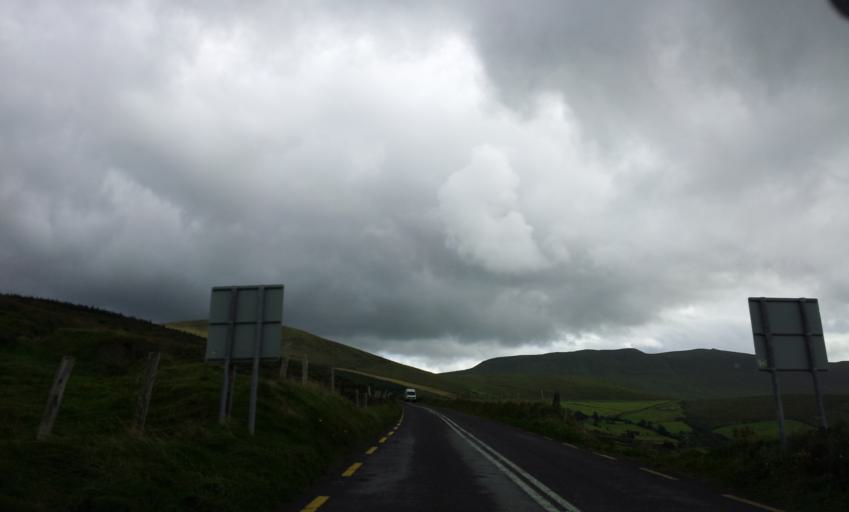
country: IE
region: Munster
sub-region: Ciarrai
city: Killorglin
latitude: 52.2134
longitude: -9.9381
